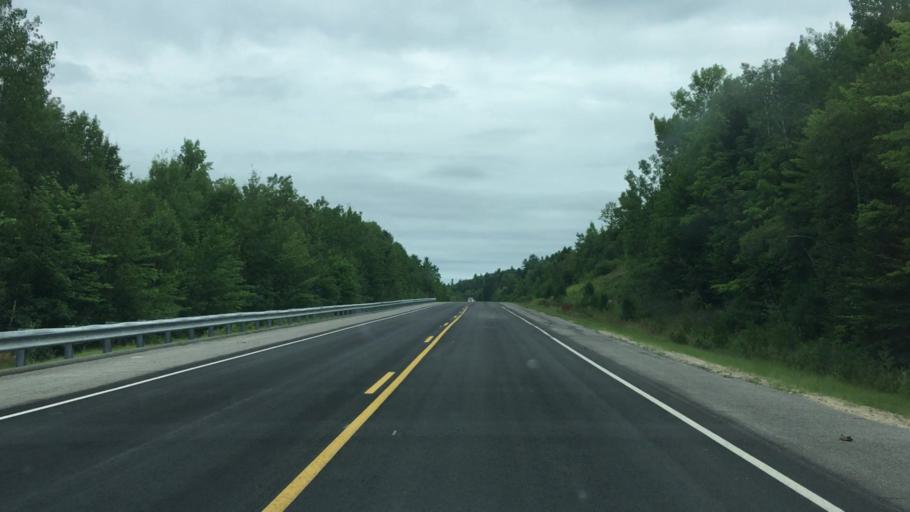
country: US
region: Maine
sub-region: Washington County
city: Cherryfield
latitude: 44.8912
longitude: -67.8563
